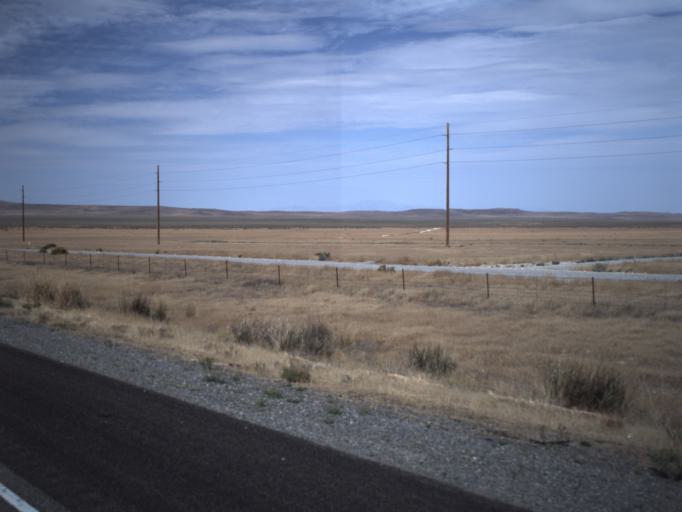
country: US
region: Utah
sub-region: Tooele County
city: Grantsville
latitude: 40.7547
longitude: -113.0330
